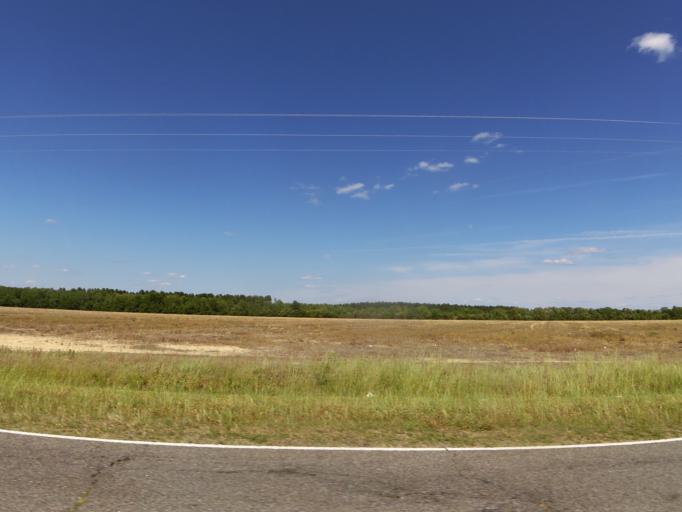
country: US
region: South Carolina
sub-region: Barnwell County
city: Williston
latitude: 33.4410
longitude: -81.4876
